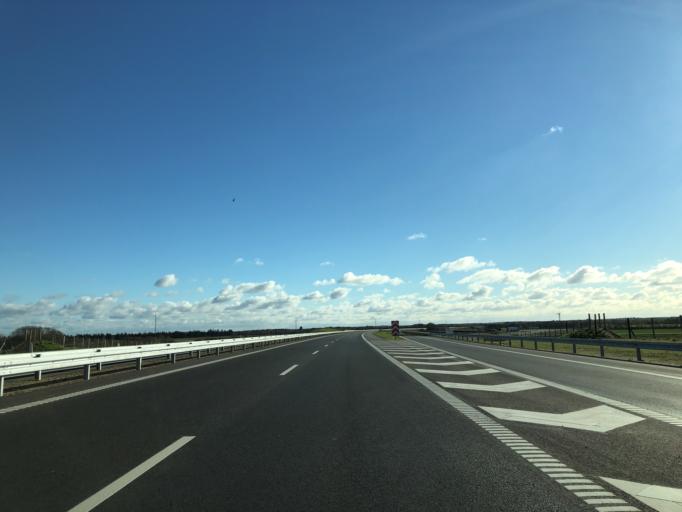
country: DK
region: Central Jutland
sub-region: Holstebro Kommune
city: Holstebro
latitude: 56.3714
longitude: 8.7133
